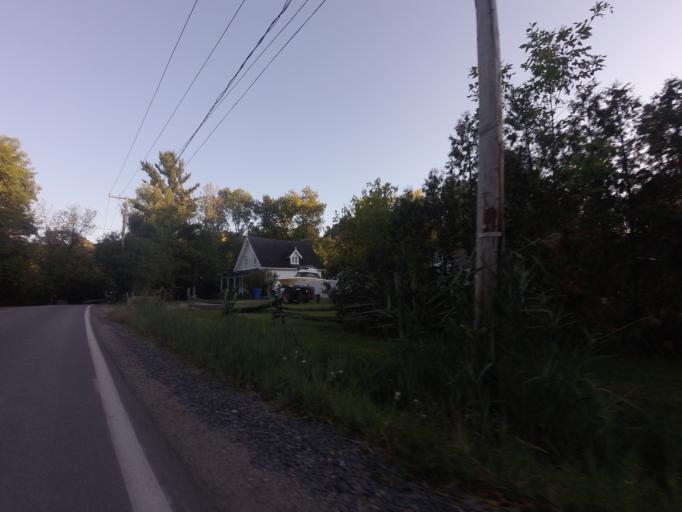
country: CA
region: Quebec
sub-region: Monteregie
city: Hudson
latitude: 45.4701
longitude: -74.1716
